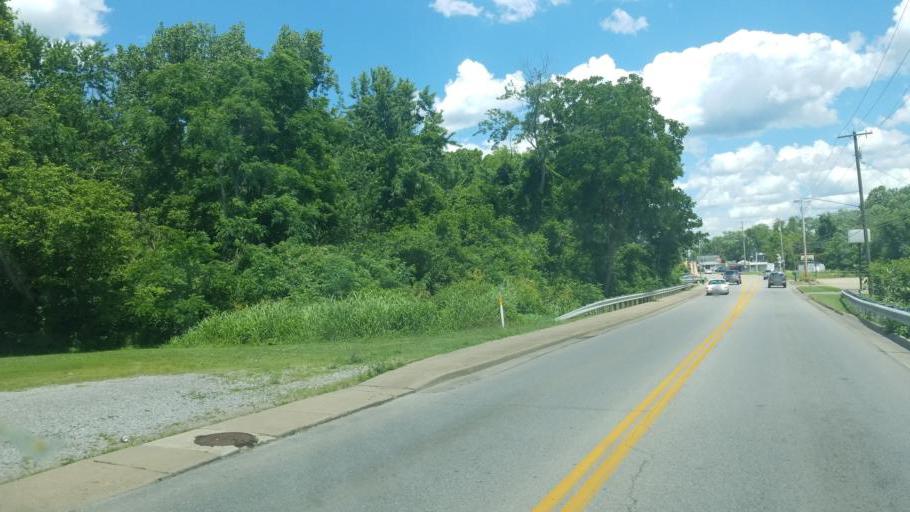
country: US
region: Ohio
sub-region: Gallia County
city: Gallipolis
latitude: 38.8169
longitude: -82.1878
